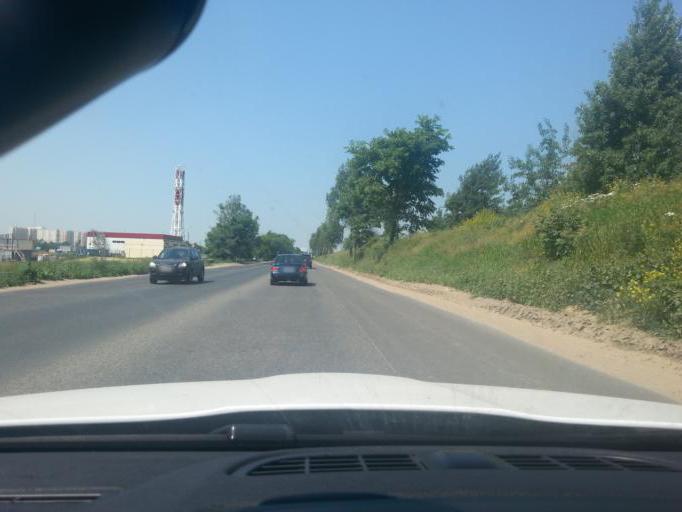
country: RU
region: Moscow
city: Nekrasovka
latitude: 55.7098
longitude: 37.9605
